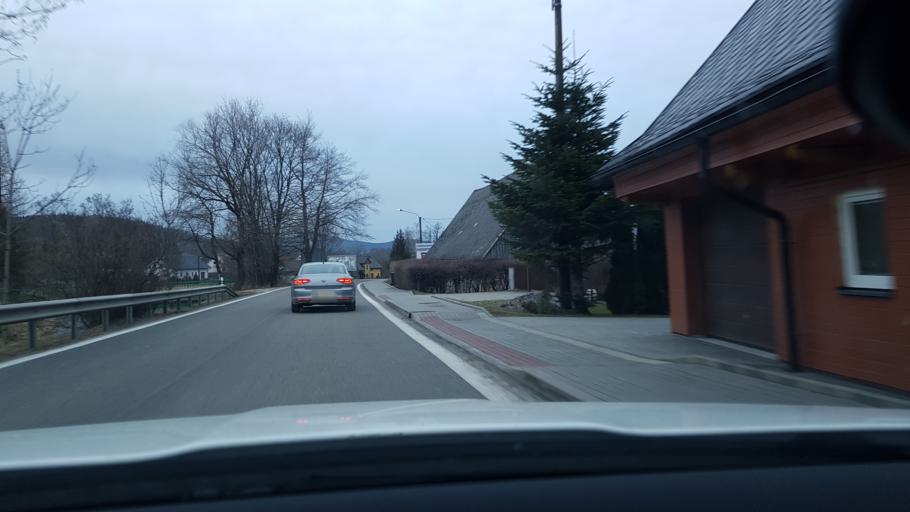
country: CZ
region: Olomoucky
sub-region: Okres Jesenik
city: Jesenik
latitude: 50.1656
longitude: 17.1957
